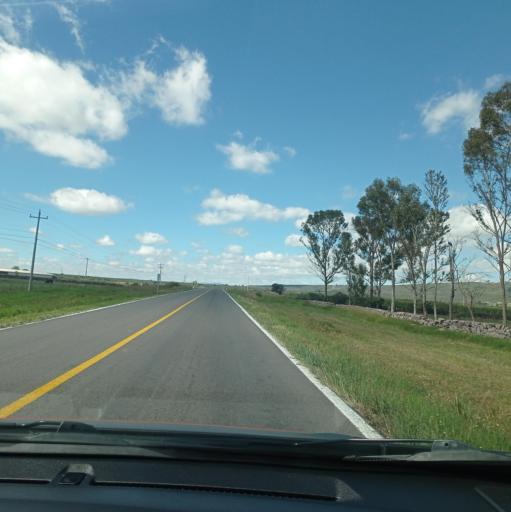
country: MX
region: Jalisco
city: San Miguel el Alto
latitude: 21.0179
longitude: -102.4649
